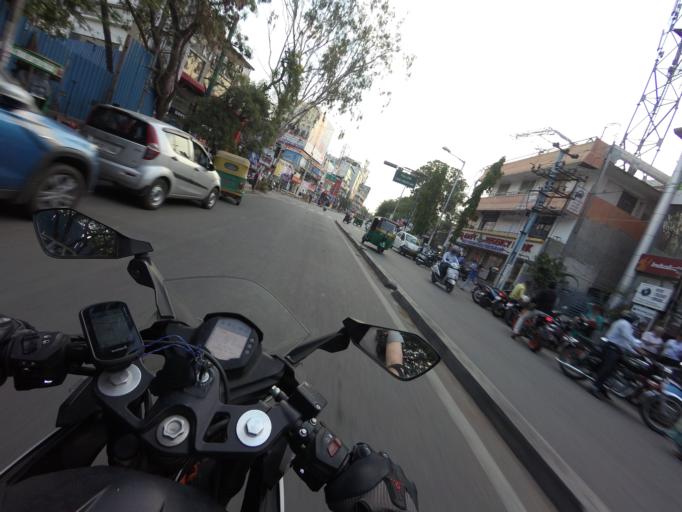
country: IN
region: Karnataka
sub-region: Bangalore Urban
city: Bangalore
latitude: 13.0230
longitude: 77.6372
